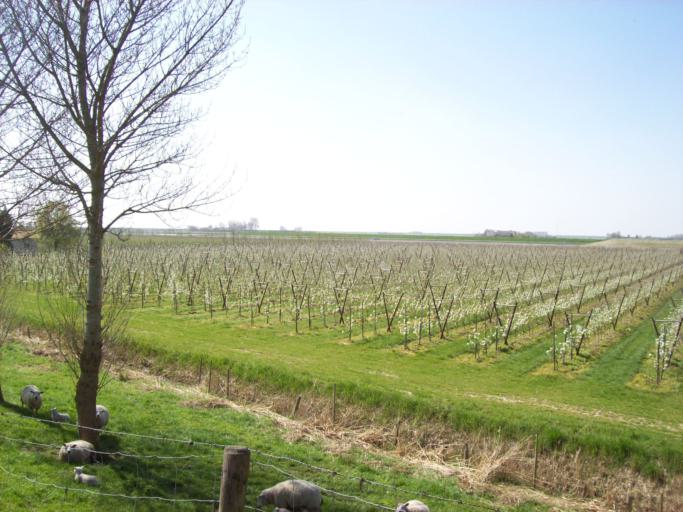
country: NL
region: Zeeland
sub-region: Gemeente Borsele
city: Borssele
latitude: 51.4295
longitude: 3.7676
